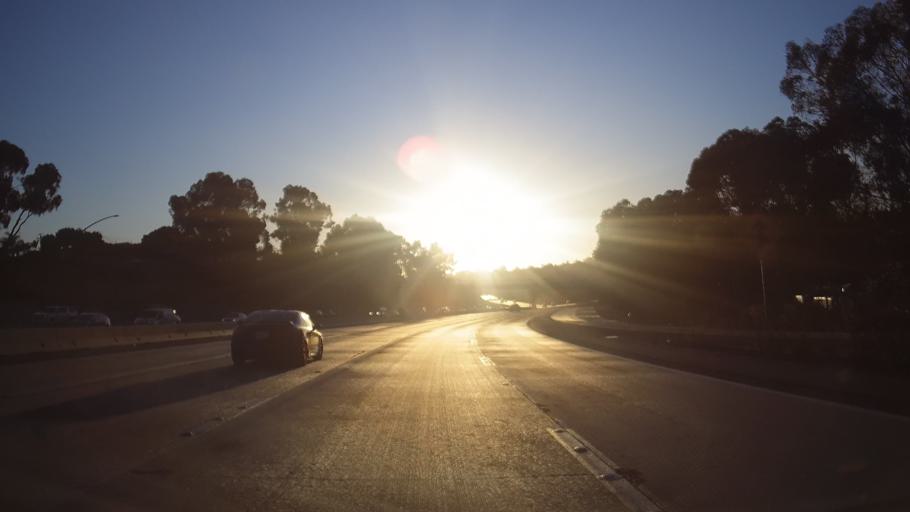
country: US
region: California
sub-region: San Diego County
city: National City
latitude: 32.7186
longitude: -117.1072
